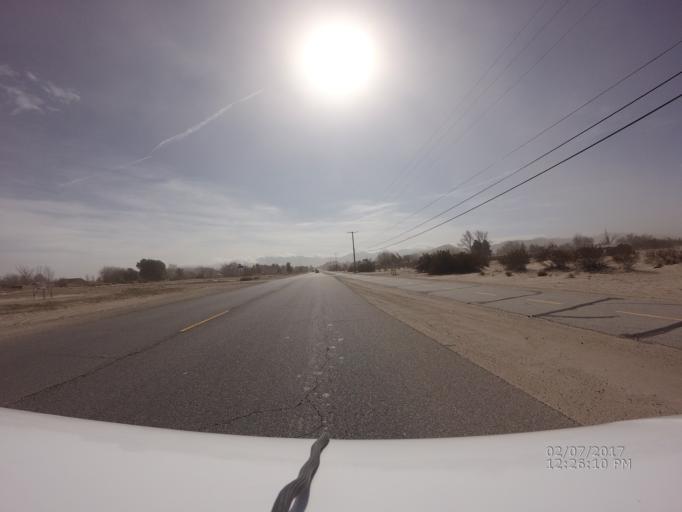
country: US
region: California
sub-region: Los Angeles County
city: Lake Los Angeles
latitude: 34.6244
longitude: -117.8270
